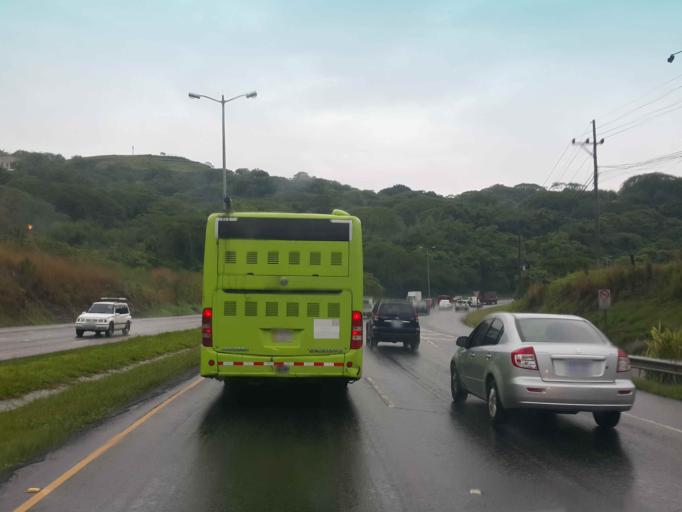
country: CR
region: San Jose
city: Santa Ana
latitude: 9.9479
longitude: -84.1778
